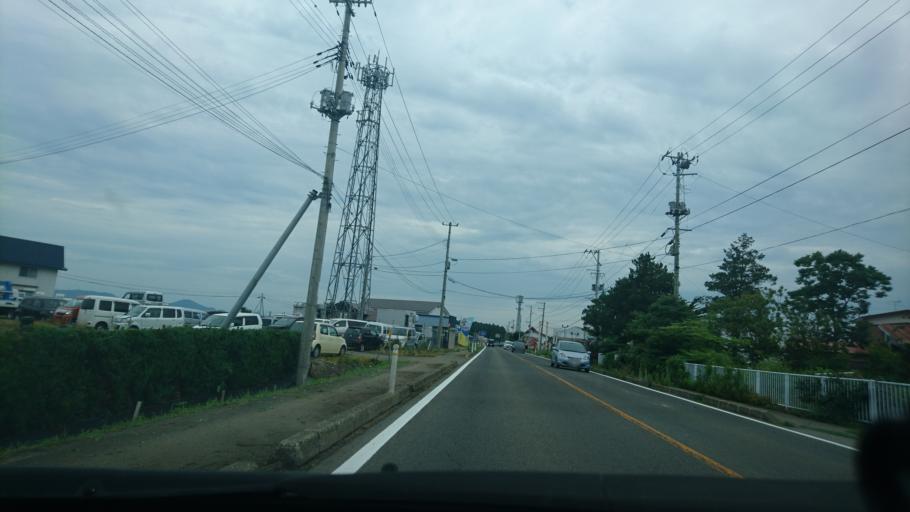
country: JP
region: Akita
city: Omagari
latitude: 39.4105
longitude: 140.5550
